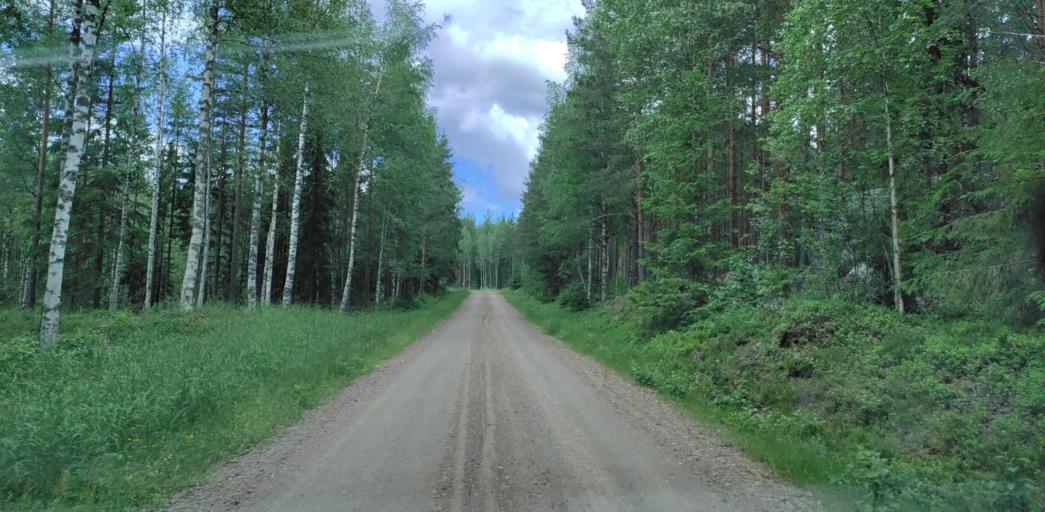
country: SE
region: Vaermland
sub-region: Hagfors Kommun
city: Ekshaerad
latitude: 60.0920
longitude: 13.4092
